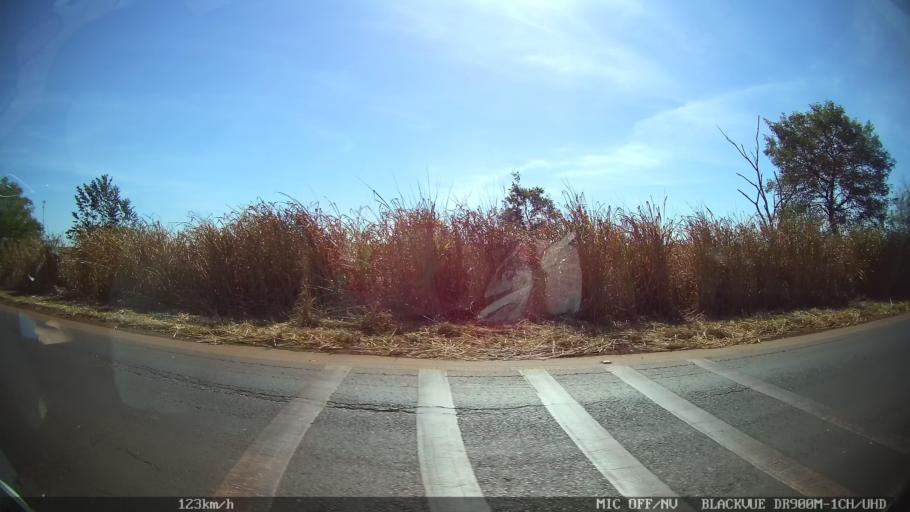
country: BR
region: Sao Paulo
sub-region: Barretos
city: Barretos
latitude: -20.4631
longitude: -48.4712
